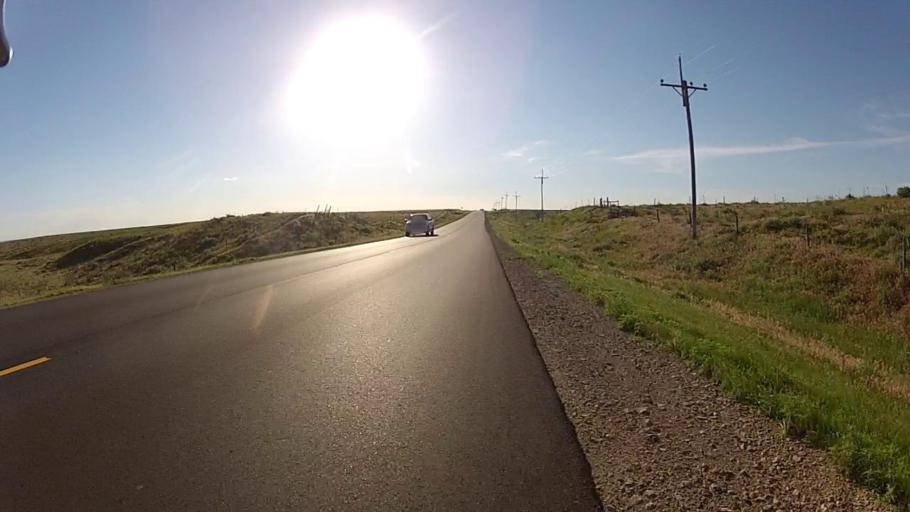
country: US
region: Kansas
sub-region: Comanche County
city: Coldwater
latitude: 37.2823
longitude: -99.1203
